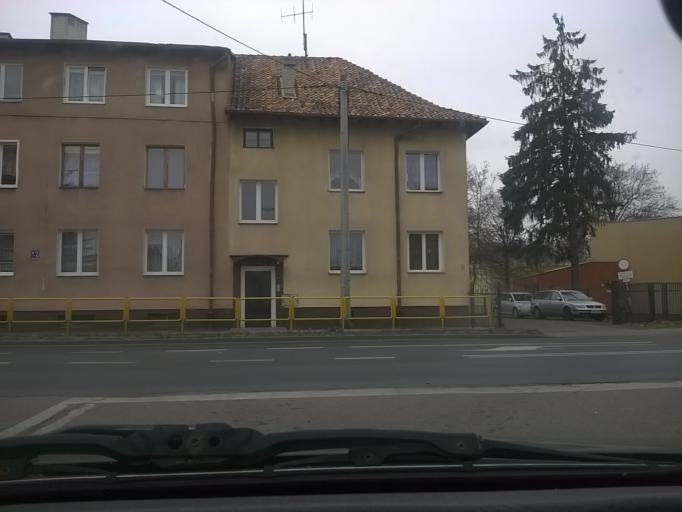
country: PL
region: Warmian-Masurian Voivodeship
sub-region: Powiat bartoszycki
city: Bartoszyce
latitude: 54.2466
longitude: 20.8071
